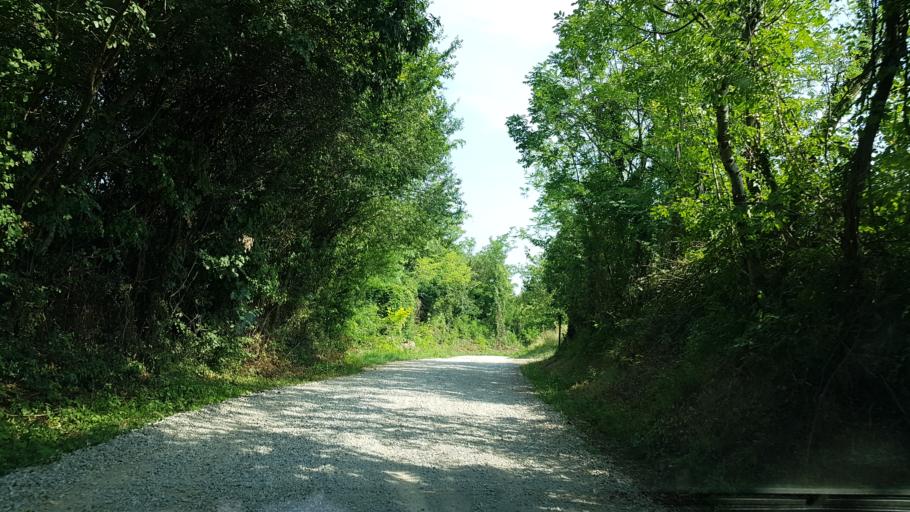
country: SI
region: Brda
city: Dobrovo
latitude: 45.9953
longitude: 13.5158
